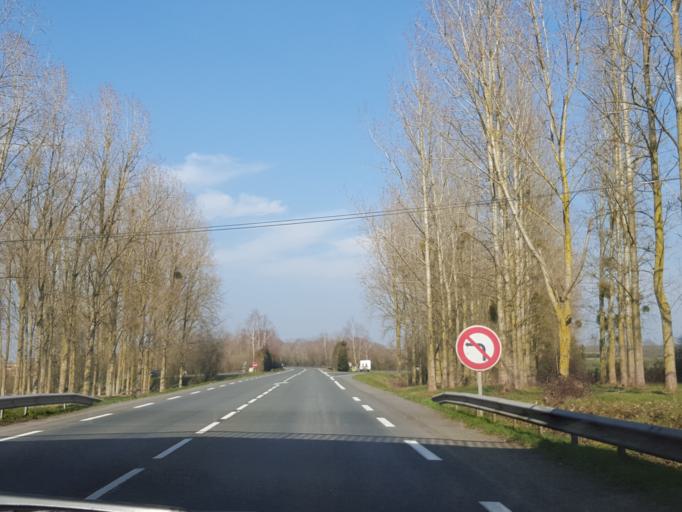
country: FR
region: Pays de la Loire
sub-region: Departement de la Vendee
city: Saint-Fulgent
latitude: 46.8468
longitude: -1.1630
